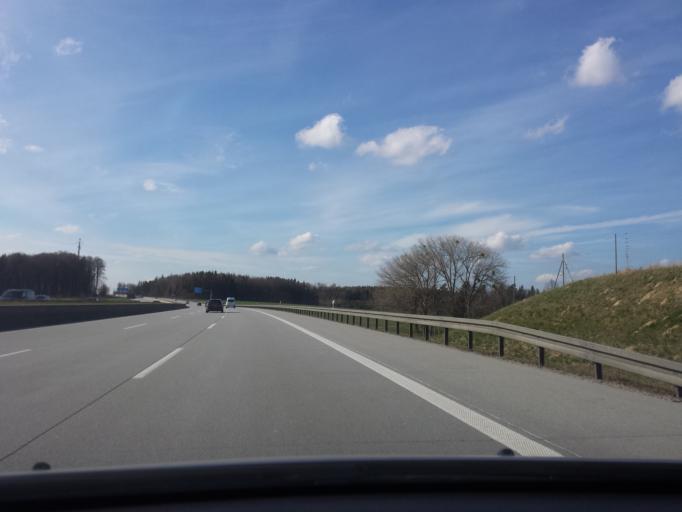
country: DE
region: Bavaria
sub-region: Upper Bavaria
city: Sulzemoos
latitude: 48.2729
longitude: 11.2852
